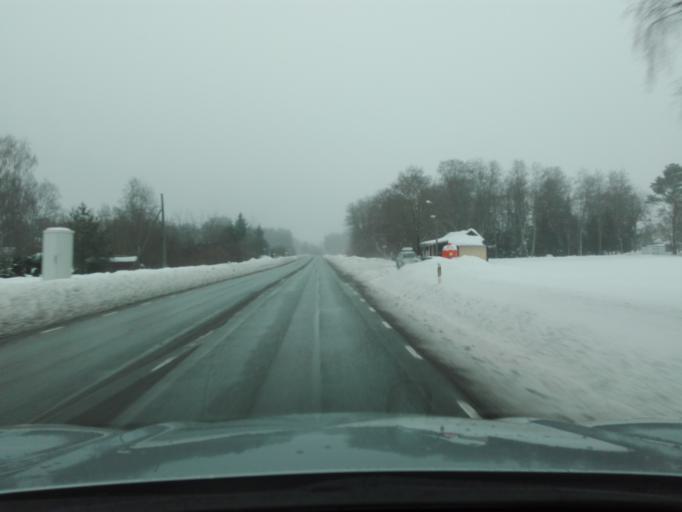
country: EE
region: Harju
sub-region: Kiili vald
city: Kiili
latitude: 59.3381
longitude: 24.7739
